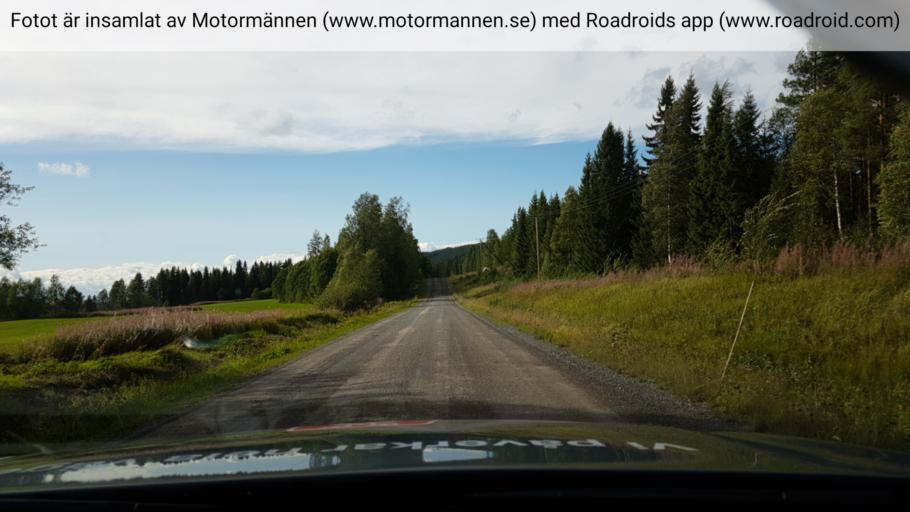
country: SE
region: Jaemtland
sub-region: Braecke Kommun
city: Braecke
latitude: 63.1923
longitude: 15.5154
